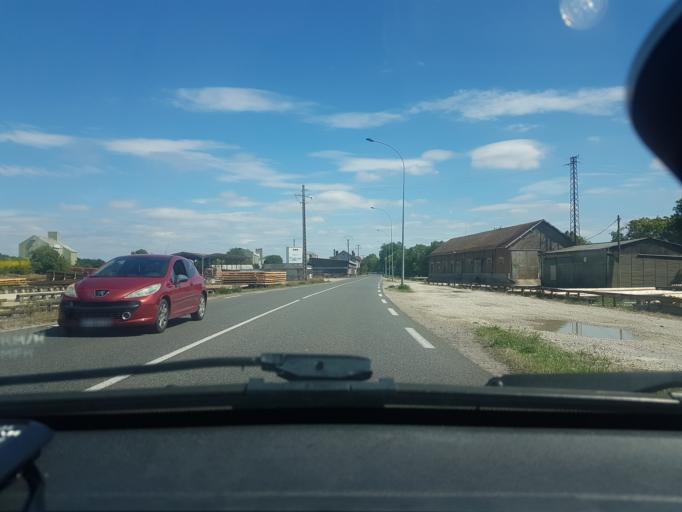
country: FR
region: Franche-Comte
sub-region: Departement de la Haute-Saone
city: Gray-la-Ville
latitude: 47.4485
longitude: 5.5673
